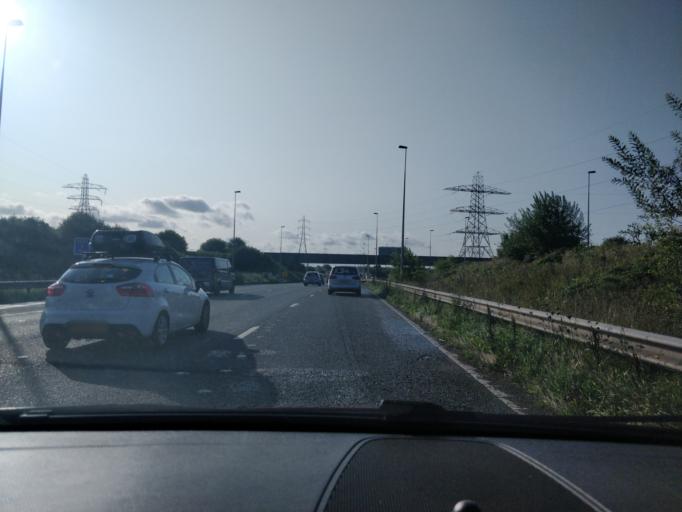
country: GB
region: England
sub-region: Sefton
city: Maghull
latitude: 53.4925
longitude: -2.9489
